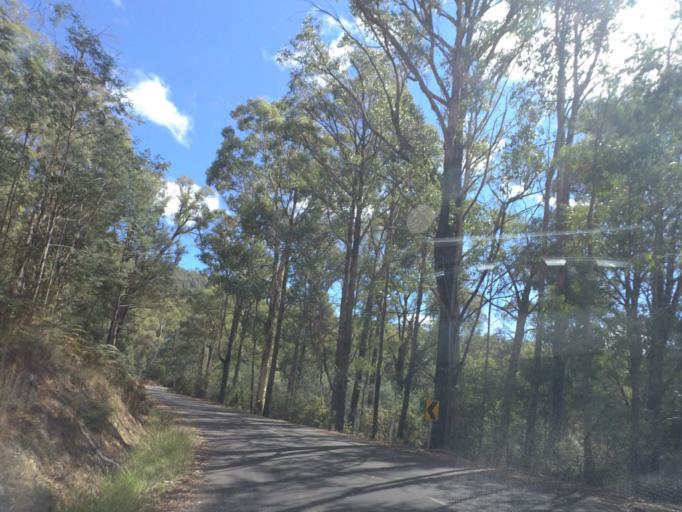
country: AU
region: Victoria
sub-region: Murrindindi
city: Alexandra
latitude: -37.3329
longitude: 145.9452
